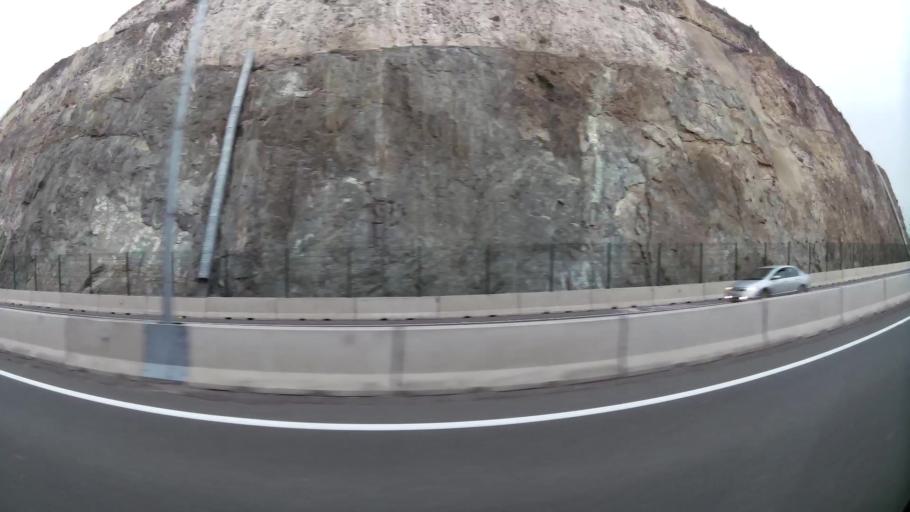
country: CL
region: Santiago Metropolitan
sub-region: Provincia de Santiago
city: Villa Presidente Frei, Nunoa, Santiago, Chile
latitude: -33.3827
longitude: -70.6047
